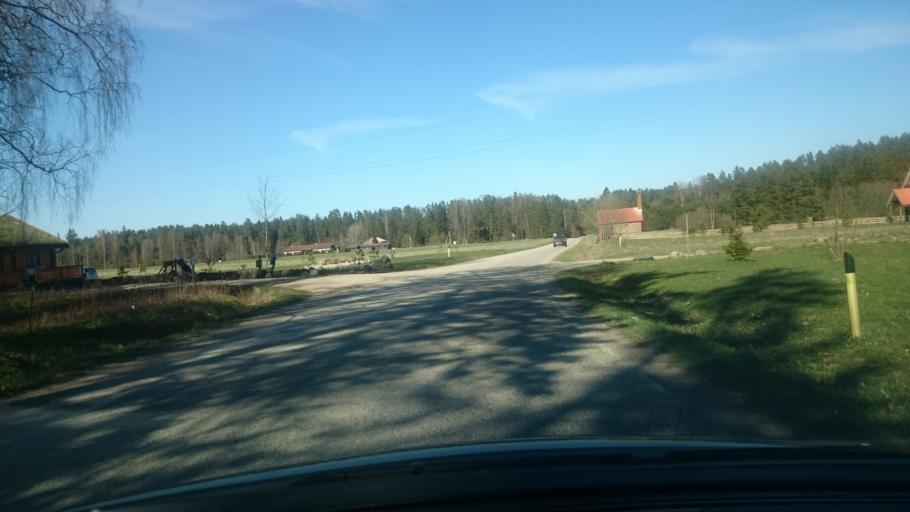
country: EE
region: Polvamaa
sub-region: Polva linn
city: Polva
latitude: 58.1361
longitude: 27.0139
